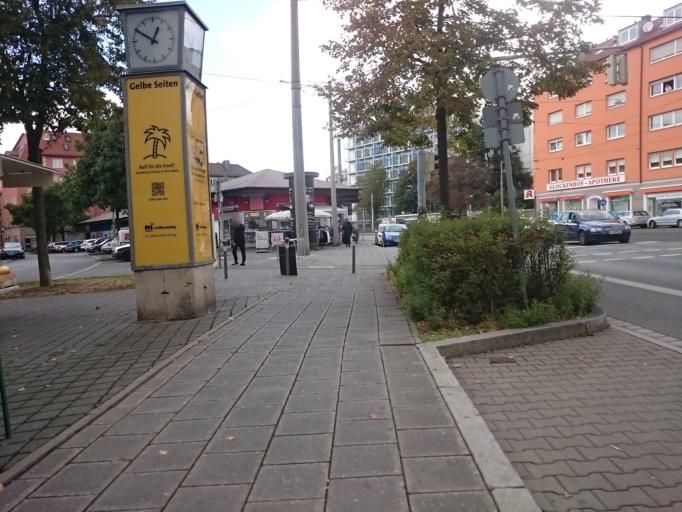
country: DE
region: Bavaria
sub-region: Regierungsbezirk Mittelfranken
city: Nuernberg
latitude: 49.4430
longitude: 11.0881
